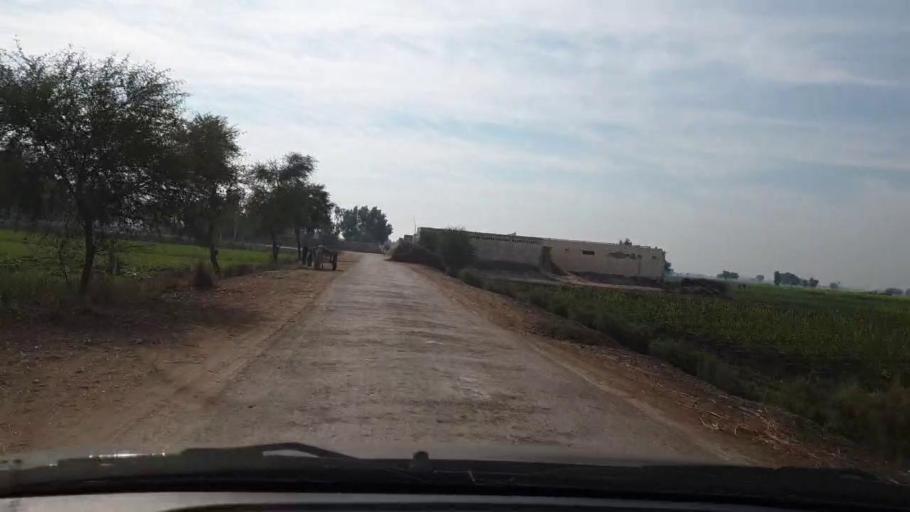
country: PK
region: Sindh
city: Shahpur Chakar
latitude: 26.1776
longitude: 68.6753
